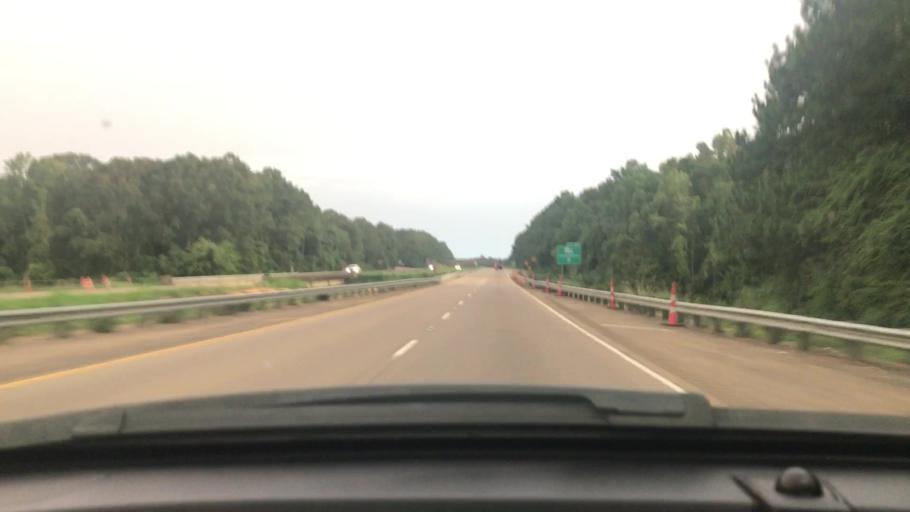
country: US
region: Louisiana
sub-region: Tangipahoa Parish
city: Kentwood
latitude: 30.8789
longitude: -90.5311
